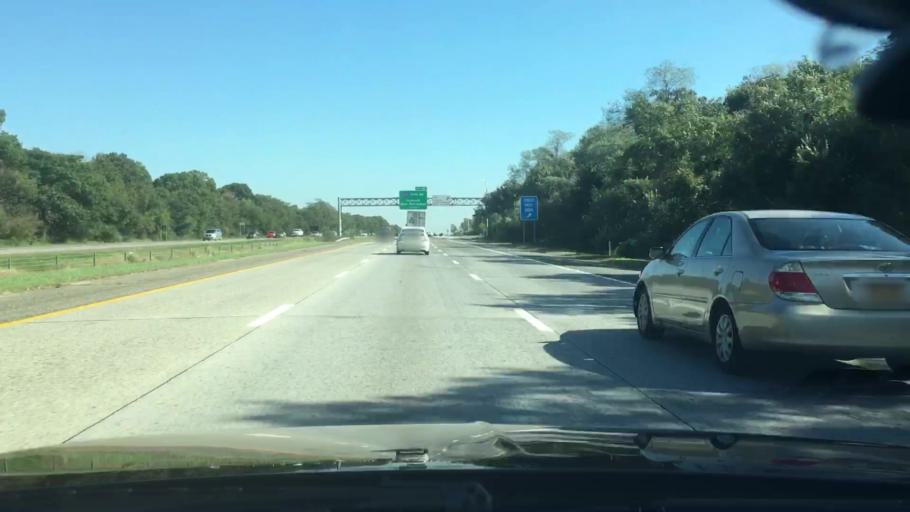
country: US
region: New York
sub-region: Suffolk County
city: Gordon Heights
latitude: 40.8258
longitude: -72.9552
